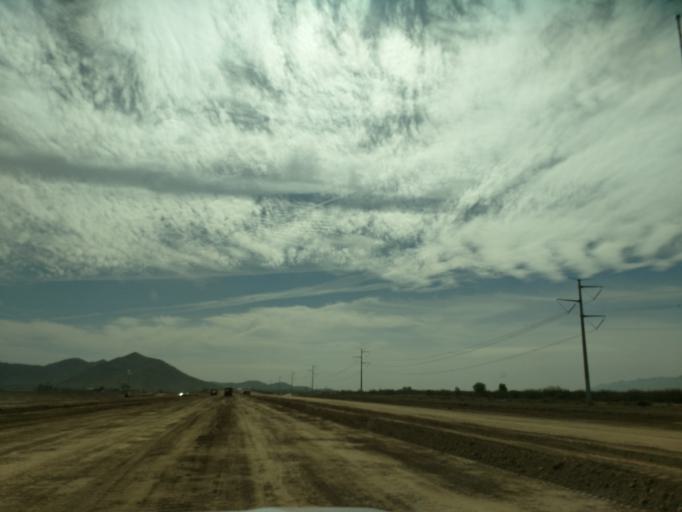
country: US
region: Arizona
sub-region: Maricopa County
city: Laveen
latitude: 33.3396
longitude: -112.1824
